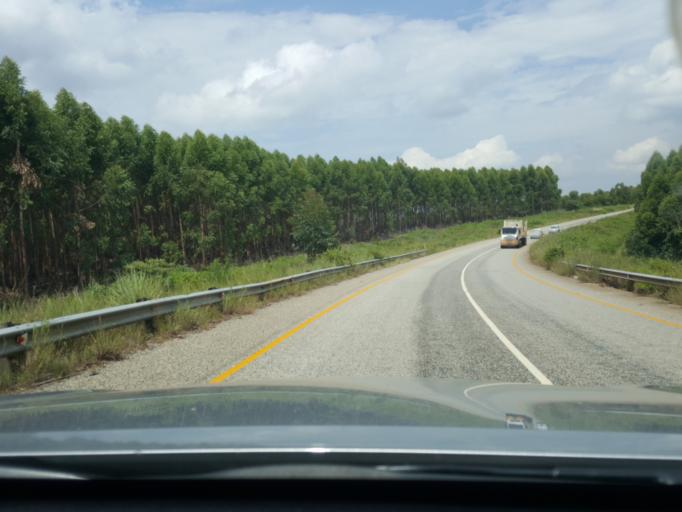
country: ZA
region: Mpumalanga
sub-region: Ehlanzeni District
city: White River
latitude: -25.1862
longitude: 30.9008
